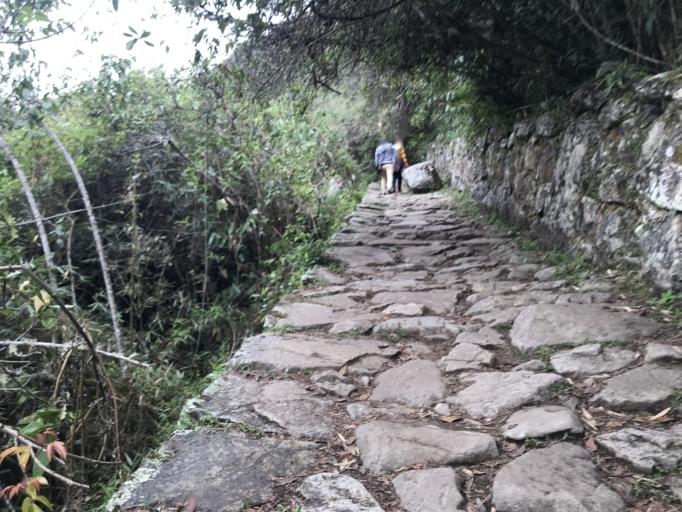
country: PE
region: Cusco
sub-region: Provincia de La Convencion
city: Santa Teresa
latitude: -13.1705
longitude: -72.5389
